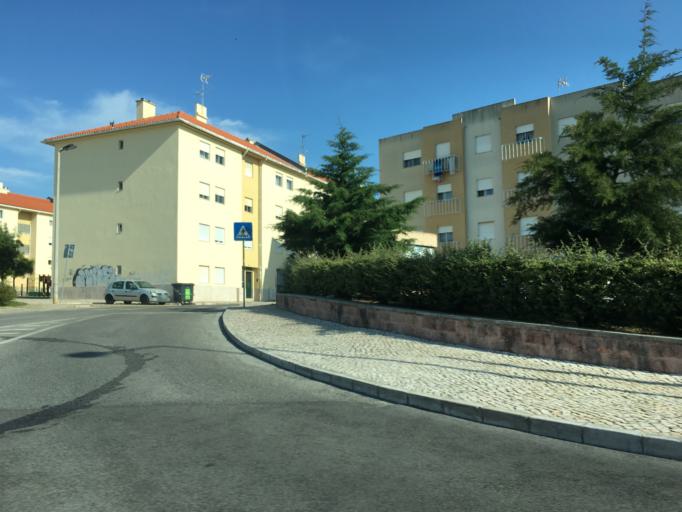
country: PT
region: Lisbon
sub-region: Cascais
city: Alcabideche
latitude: 38.7349
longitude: -9.3902
